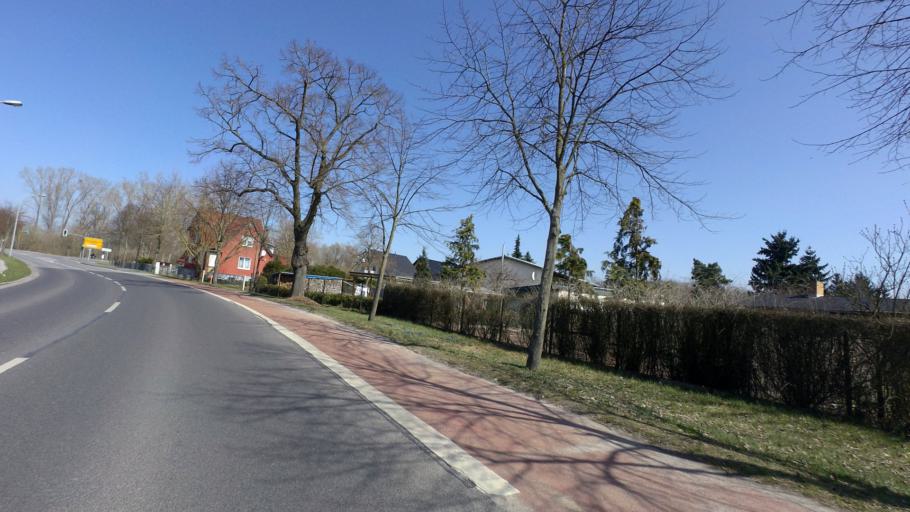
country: DE
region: Brandenburg
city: Oranienburg
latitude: 52.7723
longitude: 13.2473
